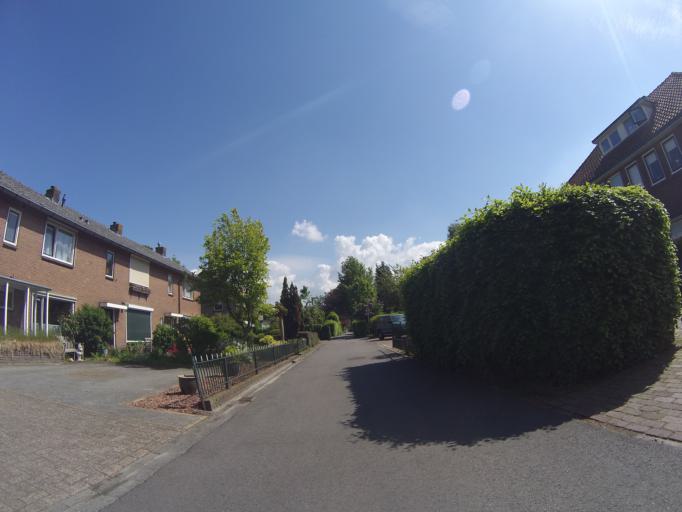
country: NL
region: Utrecht
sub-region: Gemeente Soest
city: Soest
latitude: 52.1793
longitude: 5.3072
